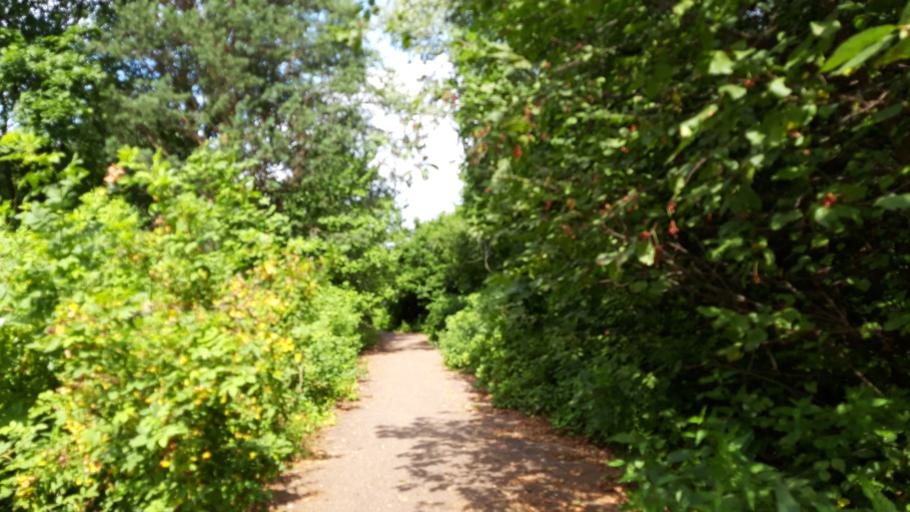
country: RU
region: Tverskaya
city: Konakovo
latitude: 56.6685
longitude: 36.6842
